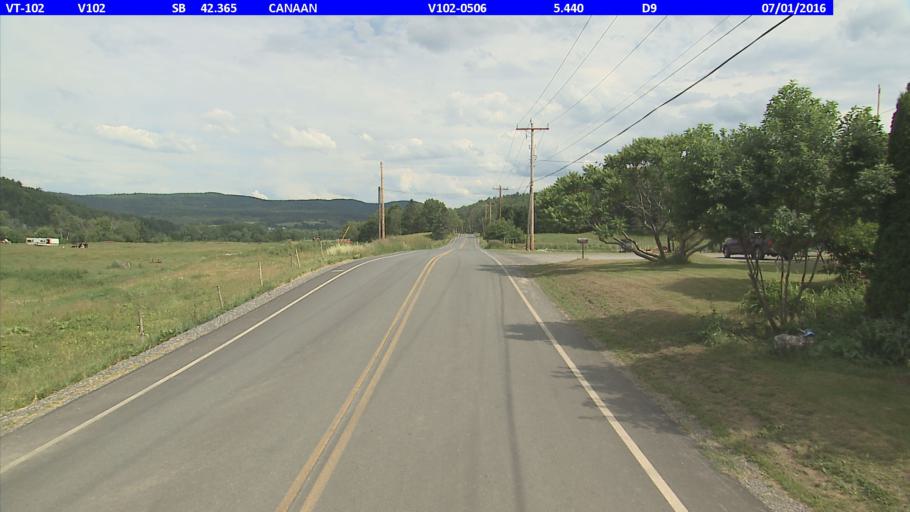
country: US
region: New Hampshire
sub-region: Coos County
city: Colebrook
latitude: 44.9777
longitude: -71.5404
